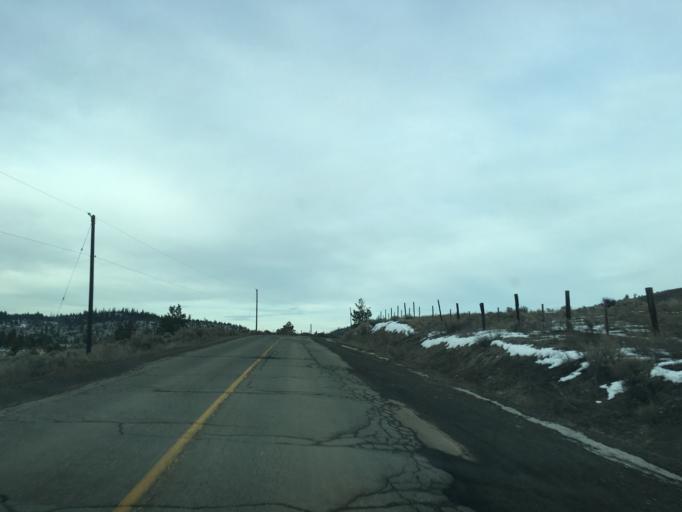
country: CA
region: British Columbia
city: Kamloops
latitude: 50.6223
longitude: -120.4432
